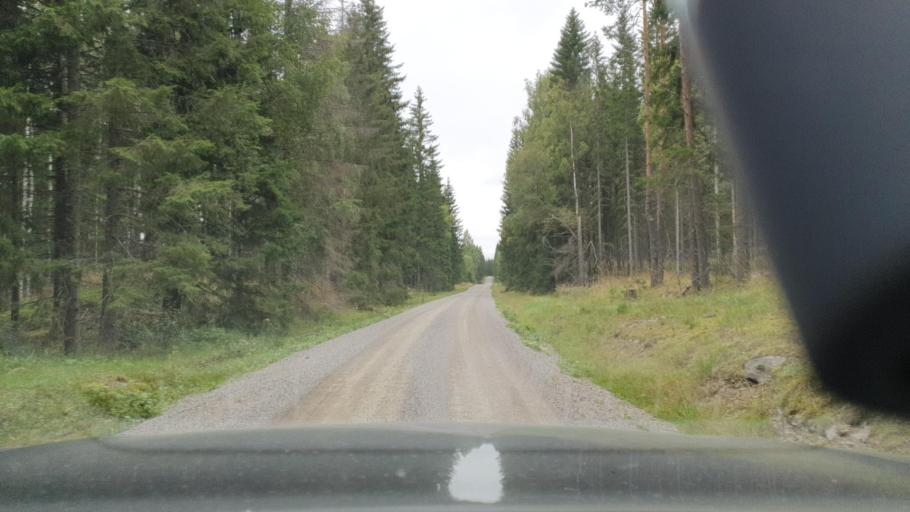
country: SE
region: Vaermland
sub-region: Eda Kommun
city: Charlottenberg
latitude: 60.0313
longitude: 12.6322
